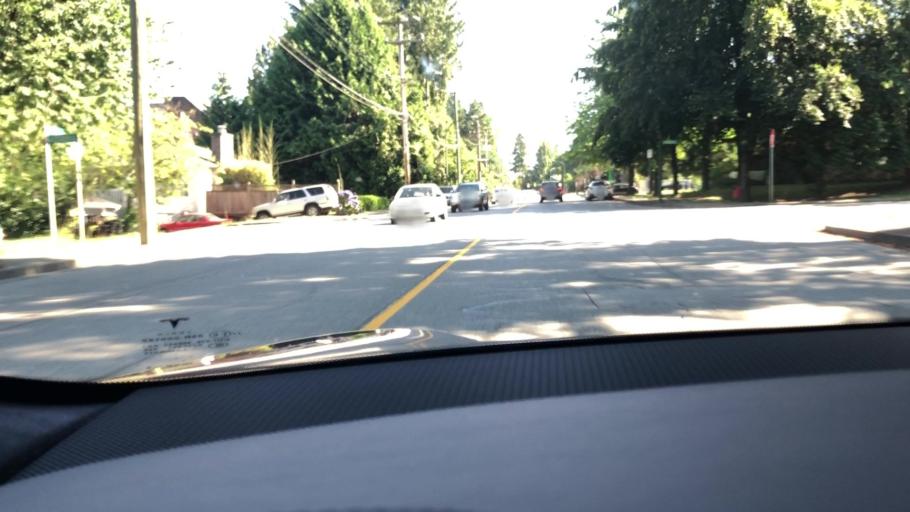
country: CA
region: British Columbia
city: Burnaby
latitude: 49.2486
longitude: -122.9747
